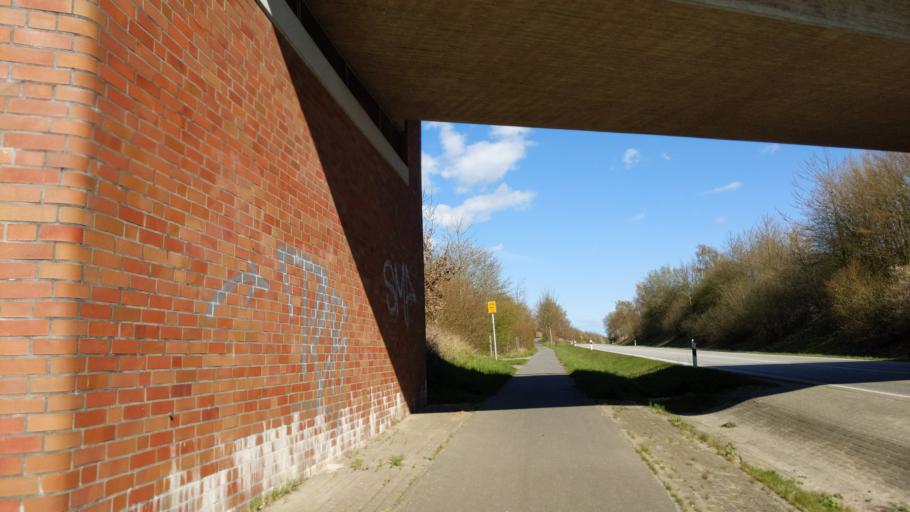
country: DE
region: Schleswig-Holstein
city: Eutin
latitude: 54.1236
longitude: 10.5876
